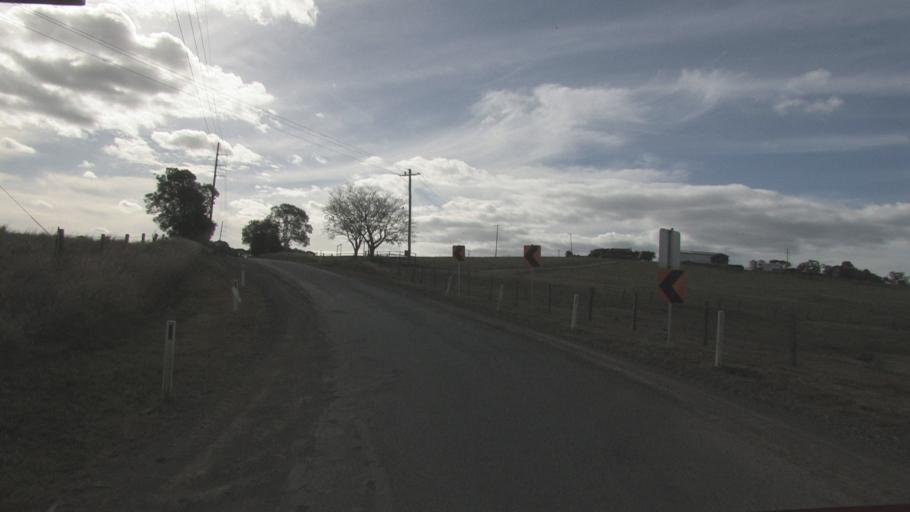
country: AU
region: Queensland
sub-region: Logan
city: Cedar Vale
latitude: -27.9116
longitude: 153.0140
